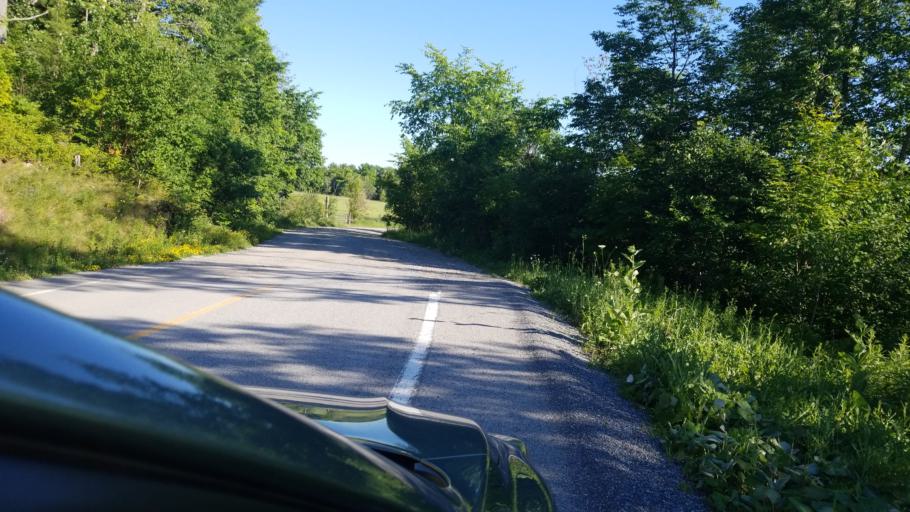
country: CA
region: Quebec
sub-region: Outaouais
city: Wakefield
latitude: 45.5949
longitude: -75.9024
